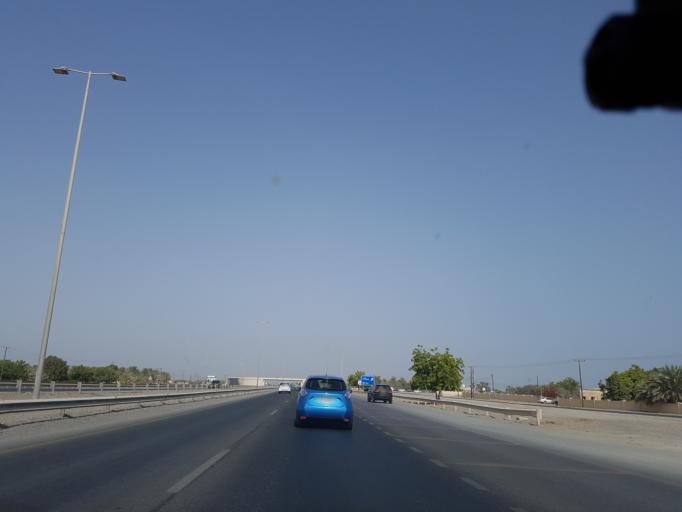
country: OM
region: Al Batinah
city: Barka'
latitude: 23.7268
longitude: 57.7201
